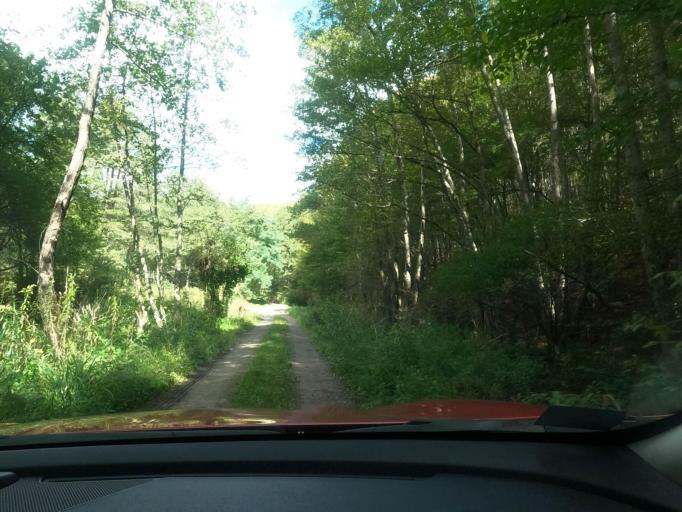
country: BA
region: Federation of Bosnia and Herzegovina
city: Velika Kladusa
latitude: 45.2376
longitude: 15.7757
